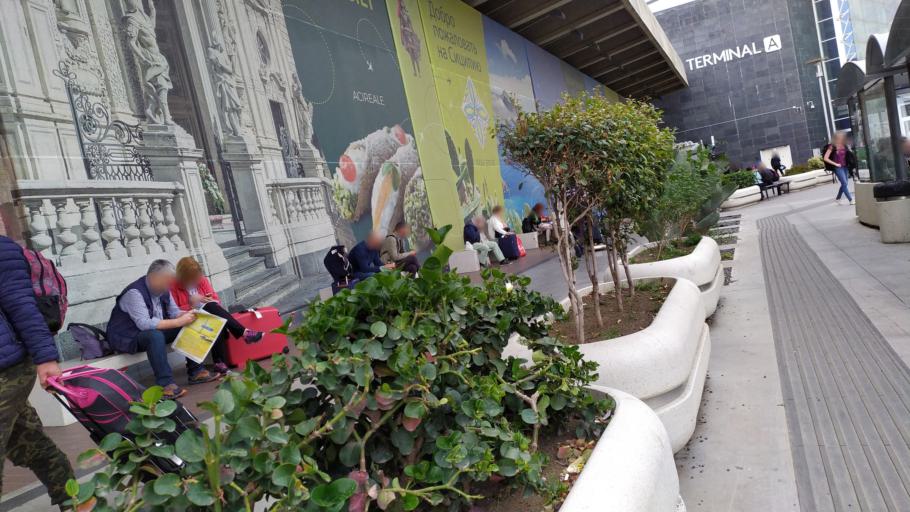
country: IT
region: Sicily
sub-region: Catania
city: Catania
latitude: 37.4703
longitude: 15.0674
